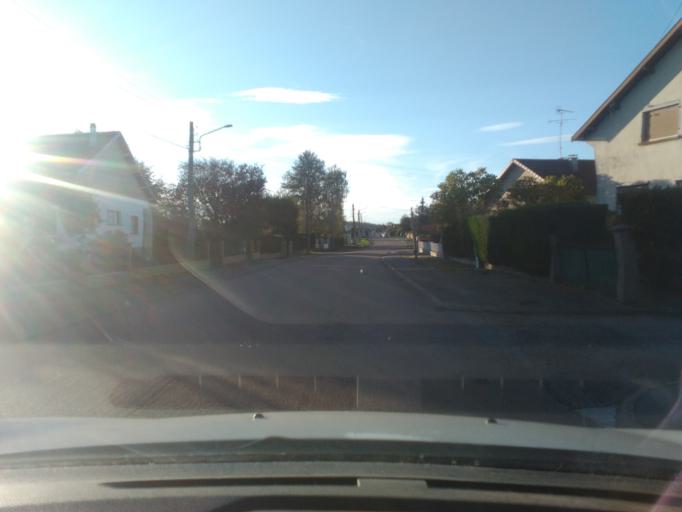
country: FR
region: Lorraine
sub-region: Departement des Vosges
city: Vincey
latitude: 48.3363
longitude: 6.3390
